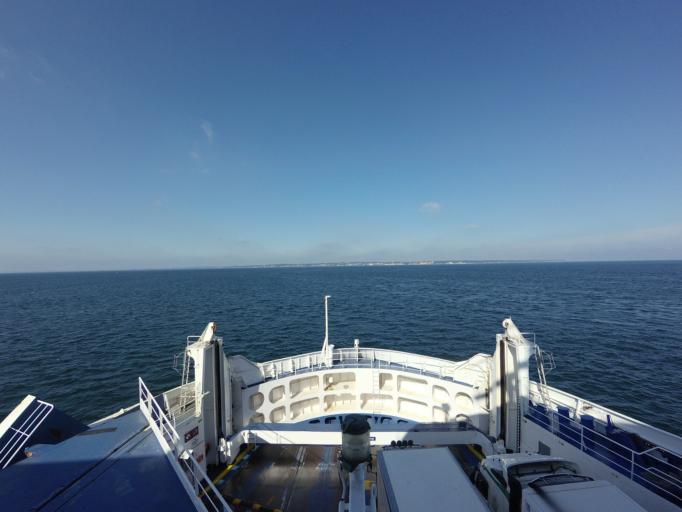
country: SE
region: Skane
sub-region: Helsingborg
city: Helsingborg
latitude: 56.0347
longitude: 12.6773
